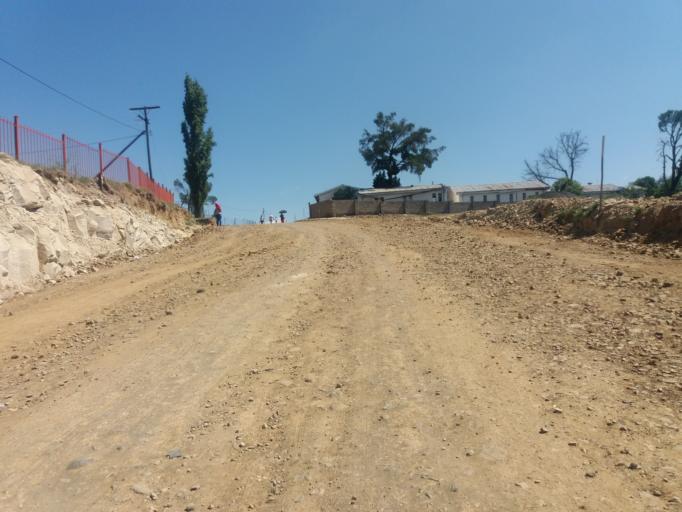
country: LS
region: Maseru
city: Maseru
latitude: -29.3179
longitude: 27.5041
